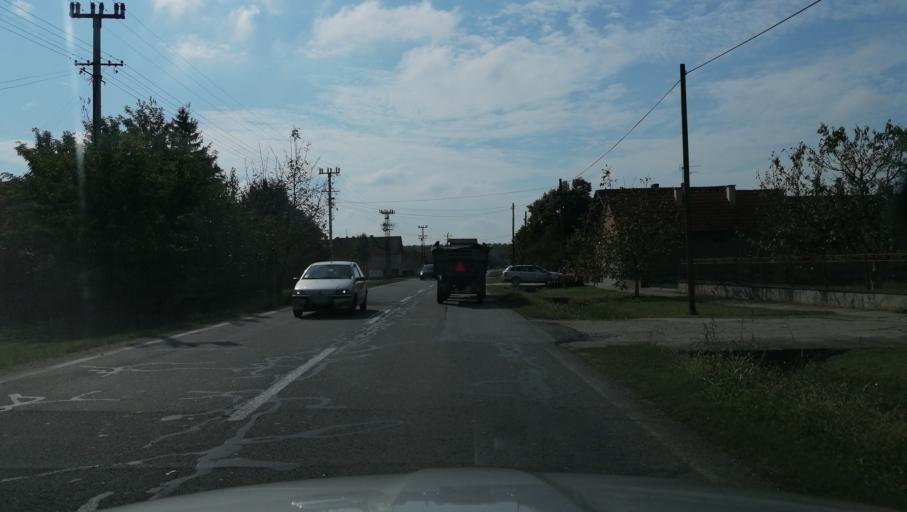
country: RS
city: Bosut
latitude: 44.9284
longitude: 19.3588
